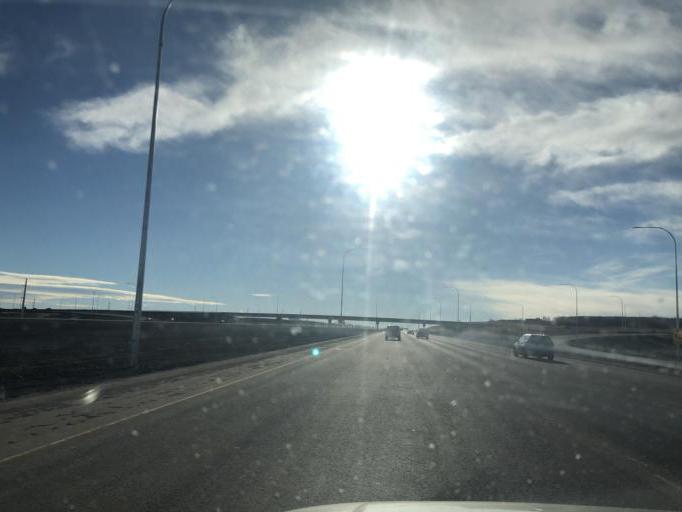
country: CA
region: Alberta
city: Calgary
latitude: 50.9796
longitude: -114.1609
